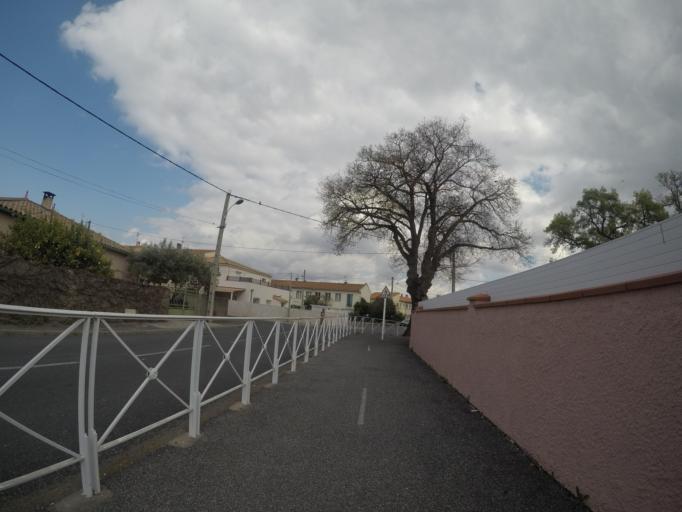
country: FR
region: Languedoc-Roussillon
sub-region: Departement des Pyrenees-Orientales
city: Le Soler
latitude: 42.6786
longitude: 2.7872
